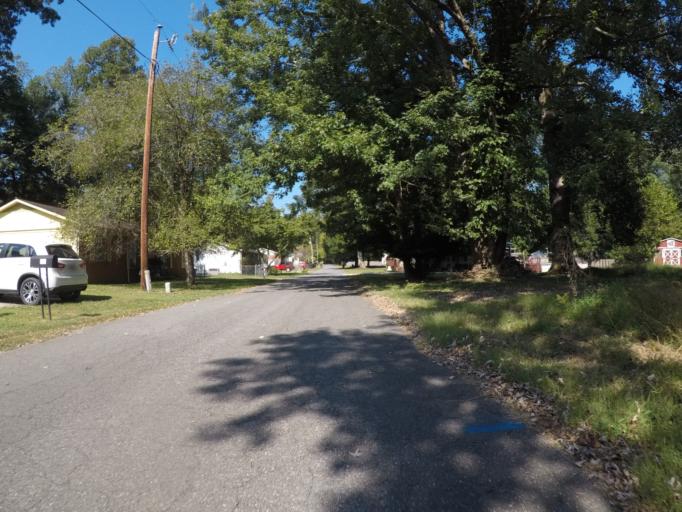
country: US
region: West Virginia
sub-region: Cabell County
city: Barboursville
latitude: 38.3742
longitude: -82.2784
